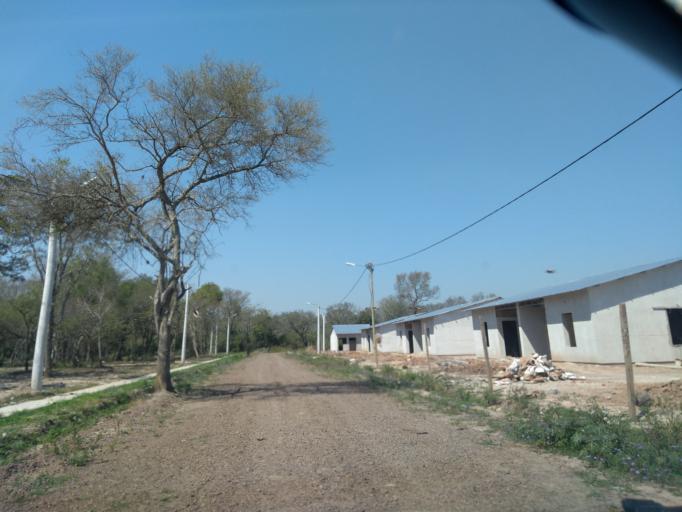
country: AR
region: Chaco
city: Resistencia
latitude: -27.4123
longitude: -58.9562
